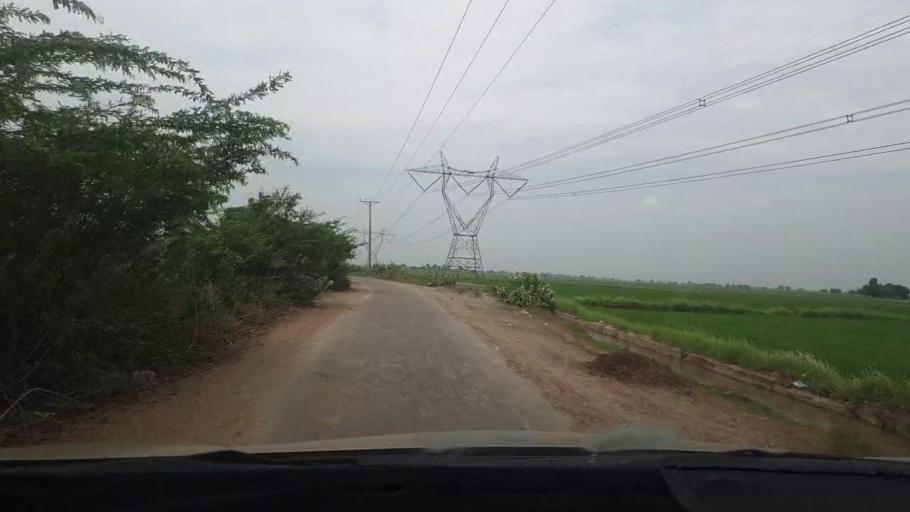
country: PK
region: Sindh
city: Naudero
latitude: 27.6795
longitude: 68.3369
